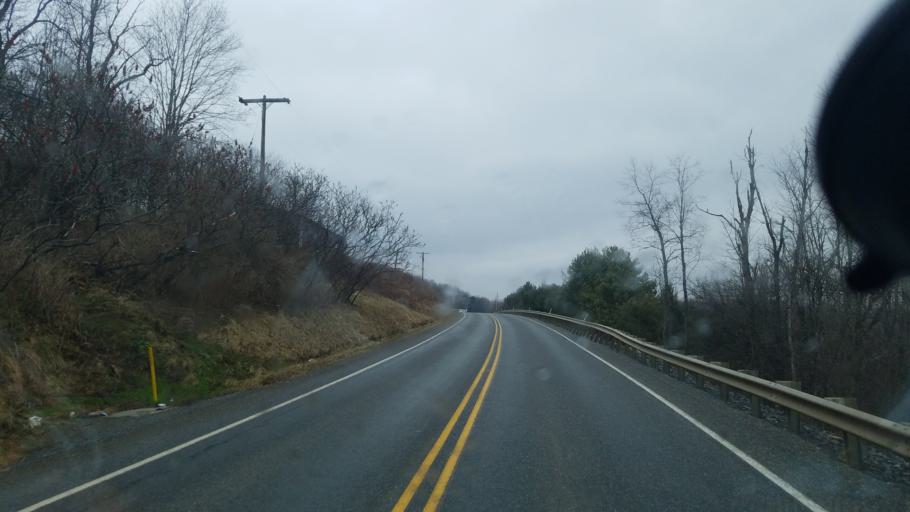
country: US
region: New York
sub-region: Allegany County
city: Wellsville
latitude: 41.9808
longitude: -77.8639
